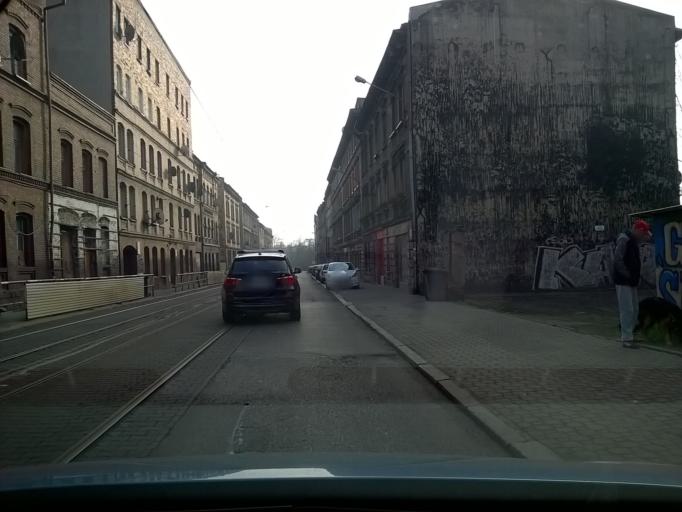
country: PL
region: Silesian Voivodeship
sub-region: Swietochlowice
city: Swietochlowice
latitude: 50.2884
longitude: 18.9475
